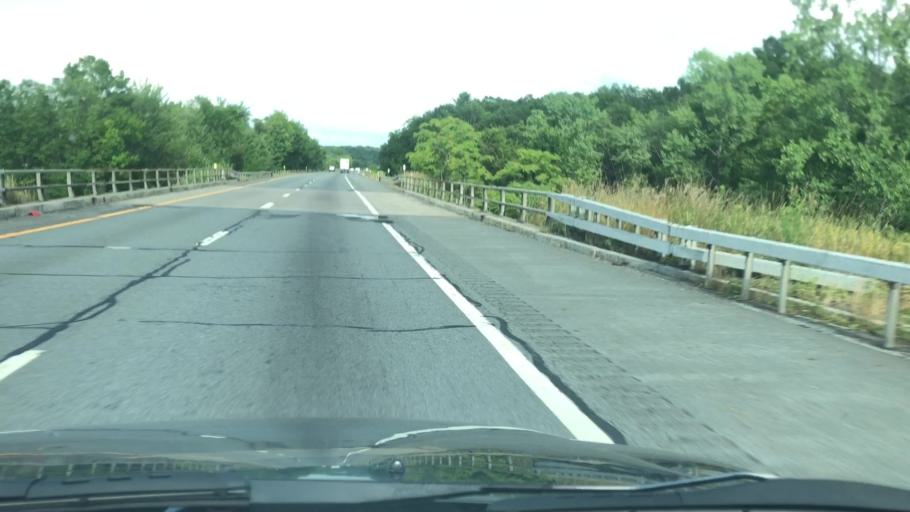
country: US
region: New York
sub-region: Orange County
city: Walden
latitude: 41.5173
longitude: -74.1821
